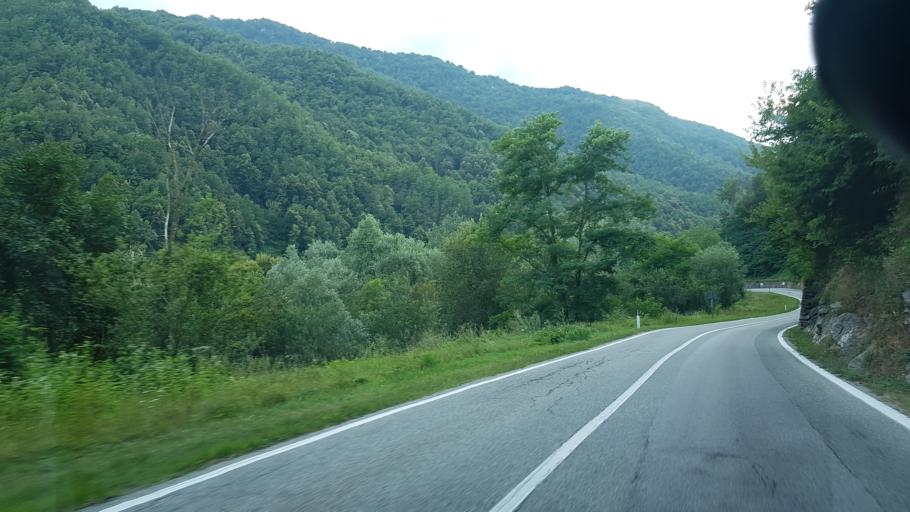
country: IT
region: Piedmont
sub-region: Provincia di Cuneo
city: Valmala
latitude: 44.5570
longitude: 7.3400
